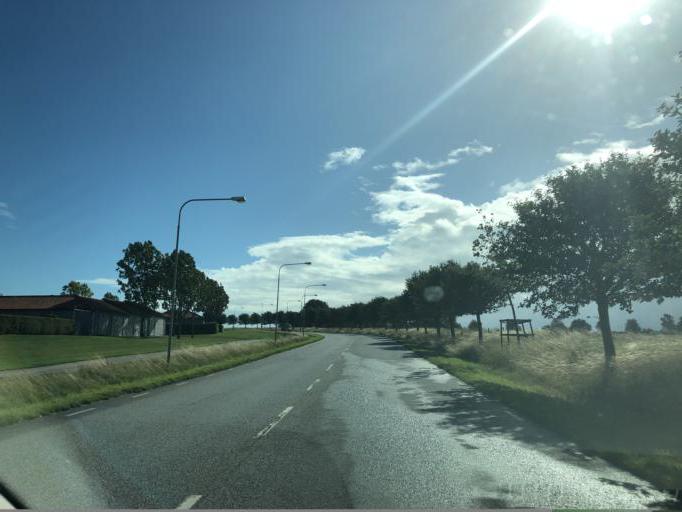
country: SE
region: Skane
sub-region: Helsingborg
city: Glumslov
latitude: 55.9386
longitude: 12.8050
